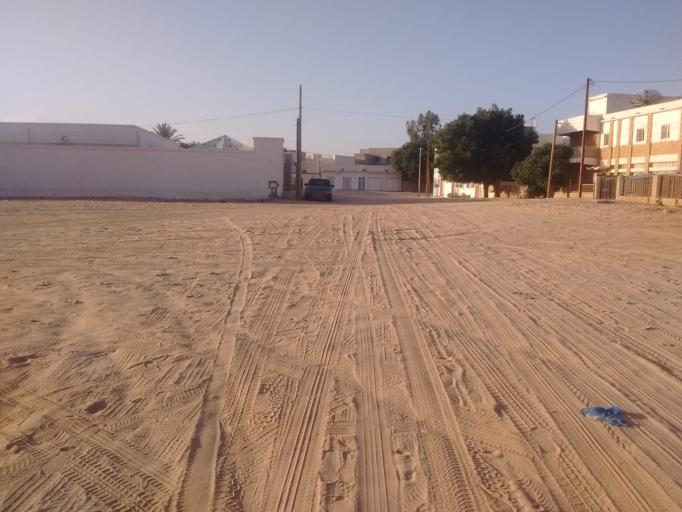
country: MR
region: Nouakchott
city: Nouakchott
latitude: 18.1002
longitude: -15.9778
